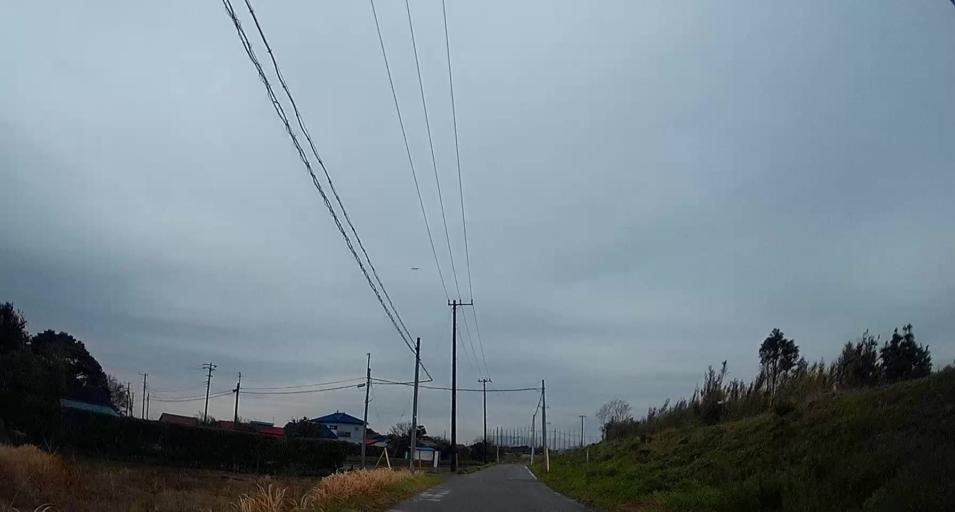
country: JP
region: Chiba
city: Kisarazu
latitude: 35.4128
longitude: 139.9085
